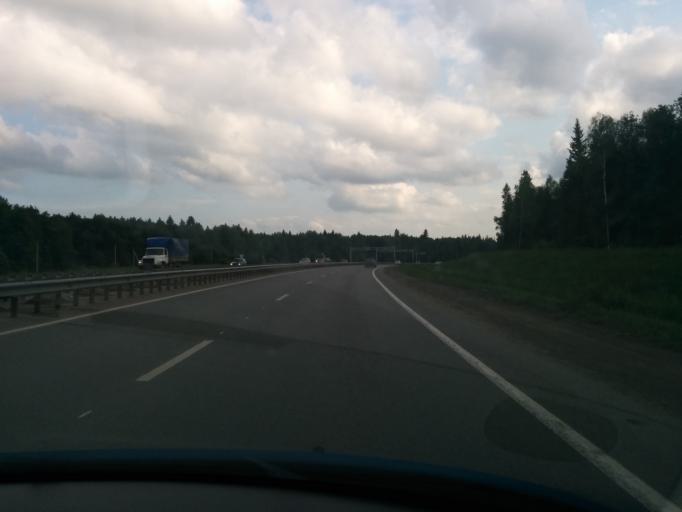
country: RU
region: Perm
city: Novyye Lyady
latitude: 58.0344
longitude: 56.4340
